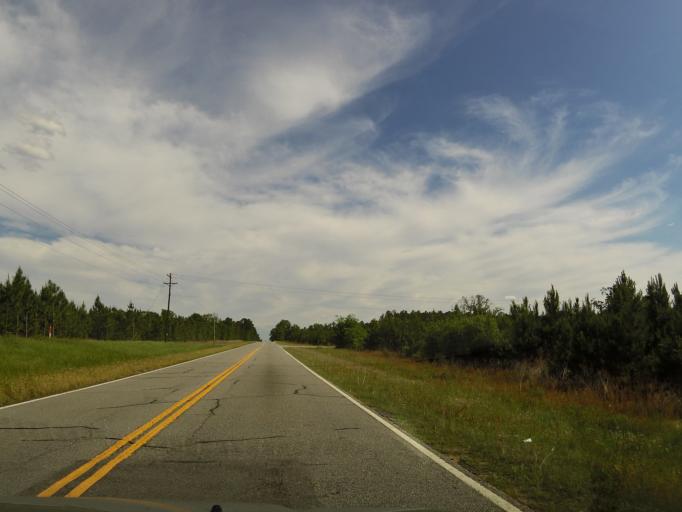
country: US
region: South Carolina
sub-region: Allendale County
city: Allendale
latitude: 33.1331
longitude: -81.1866
